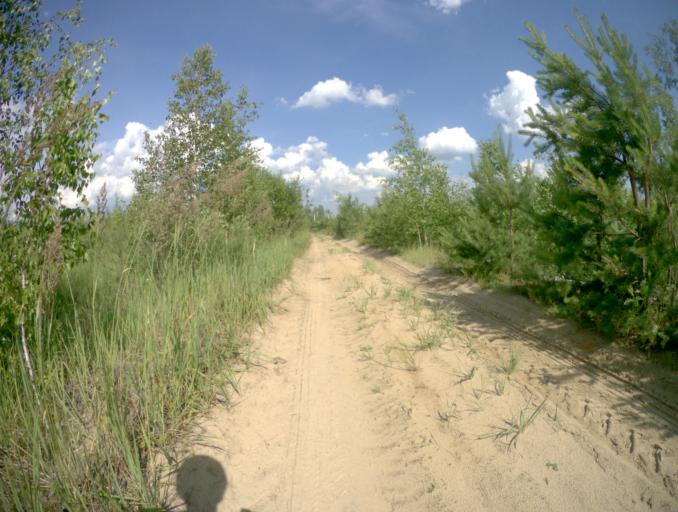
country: RU
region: Ivanovo
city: Talitsy
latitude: 56.5339
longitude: 42.2470
